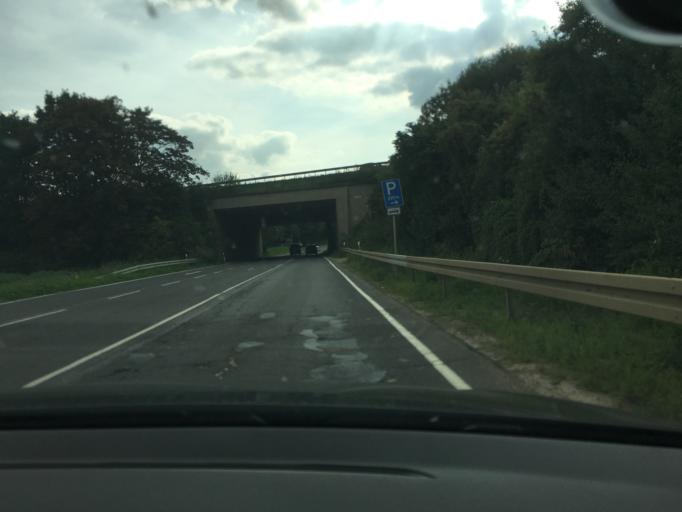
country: DE
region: North Rhine-Westphalia
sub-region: Regierungsbezirk Koln
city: Titz
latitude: 51.0410
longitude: 6.4564
